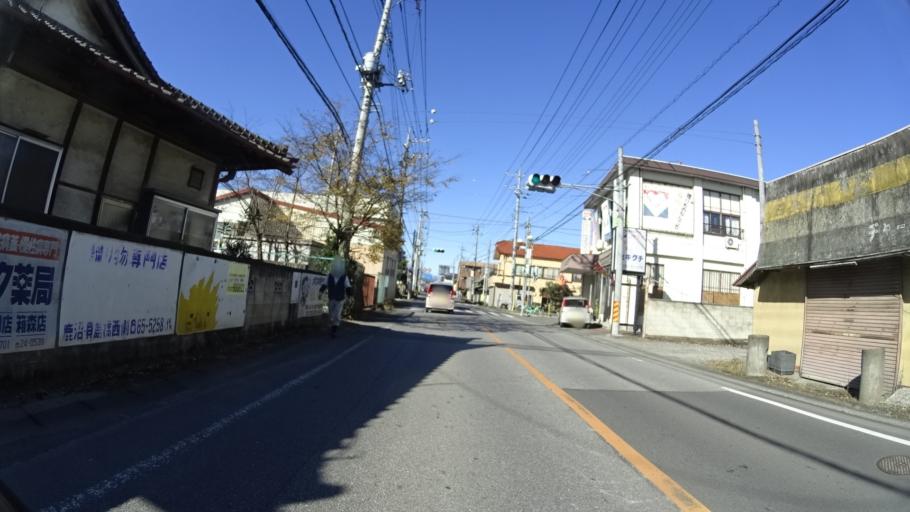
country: JP
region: Tochigi
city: Mibu
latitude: 36.4663
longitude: 139.7511
